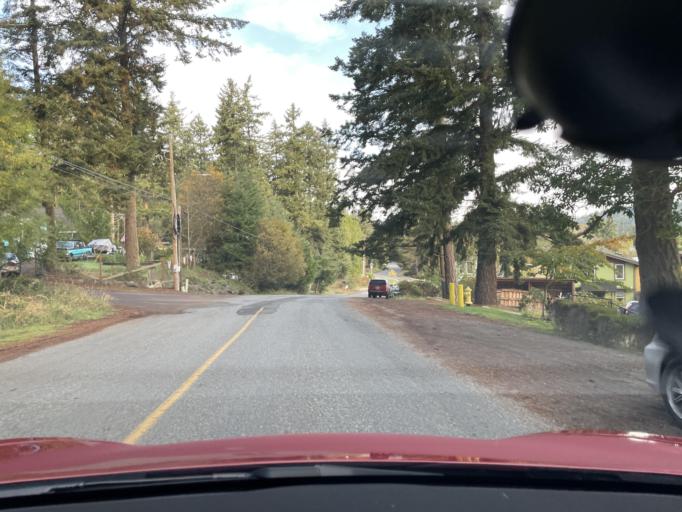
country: US
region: Washington
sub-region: San Juan County
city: Friday Harbor
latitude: 48.5351
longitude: -123.0307
